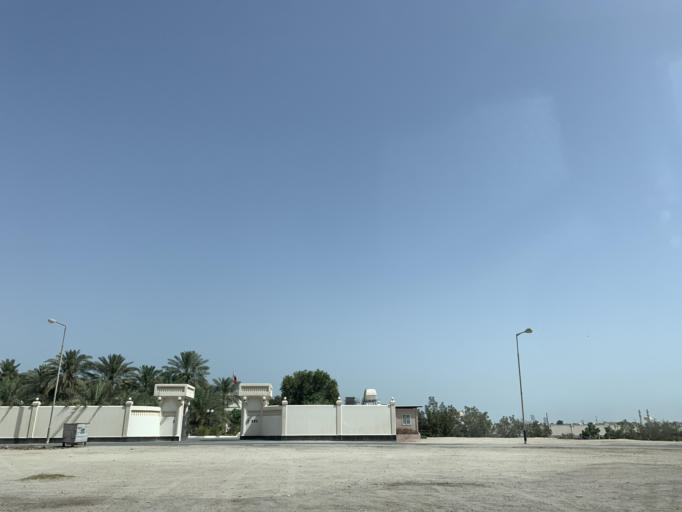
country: BH
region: Northern
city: Sitrah
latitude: 26.1466
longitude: 50.6016
